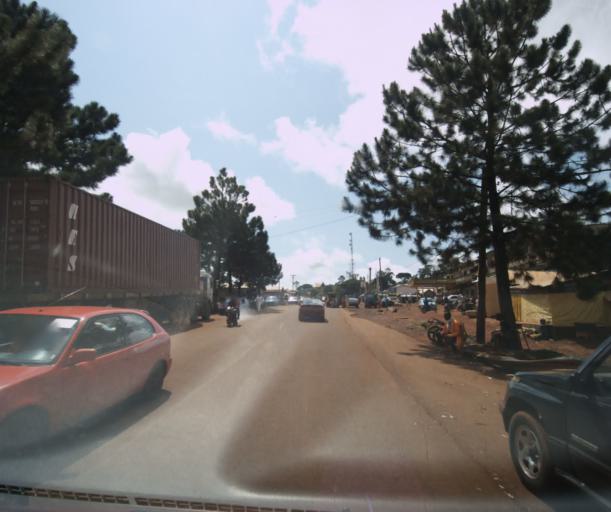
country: CM
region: West
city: Foumban
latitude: 5.7315
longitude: 10.8764
